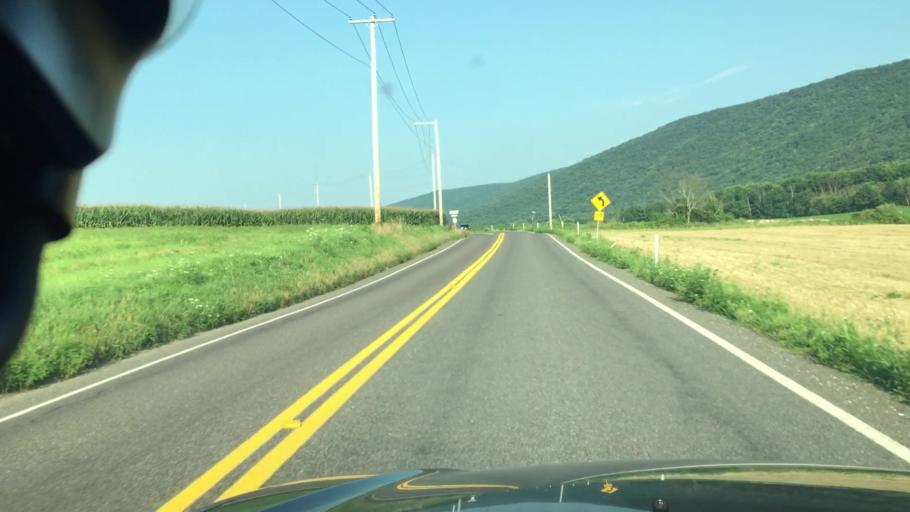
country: US
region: Pennsylvania
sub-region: Columbia County
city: Almedia
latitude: 40.9912
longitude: -76.3428
